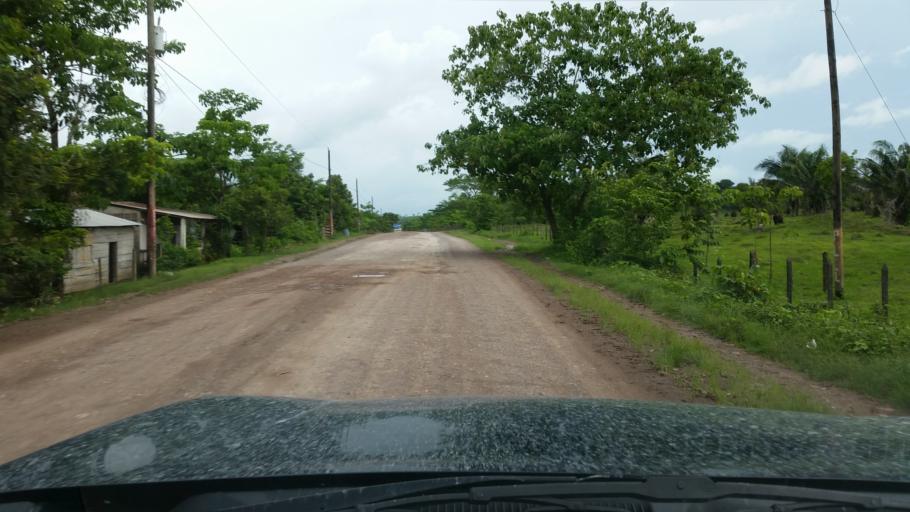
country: NI
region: Atlantico Norte (RAAN)
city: Siuna
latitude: 13.4874
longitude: -84.8447
